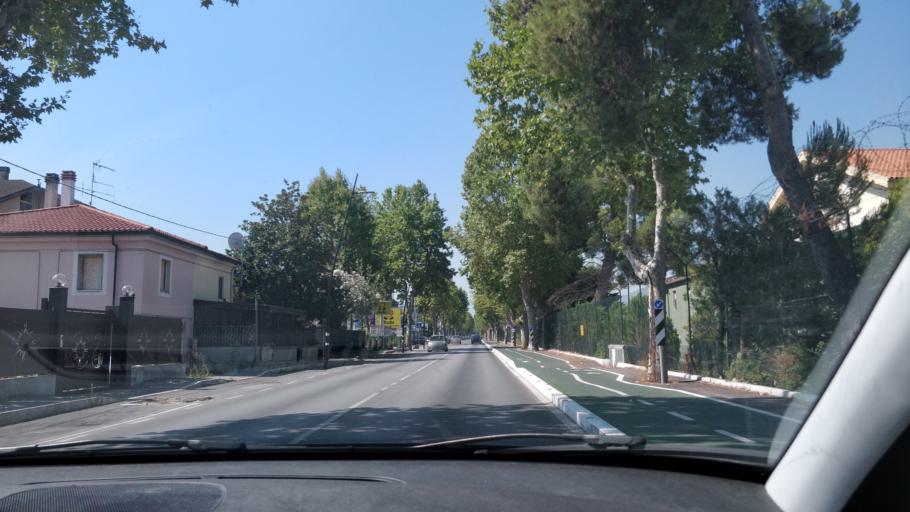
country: IT
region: Abruzzo
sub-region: Provincia di Chieti
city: Sambuceto
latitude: 42.4346
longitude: 14.1925
